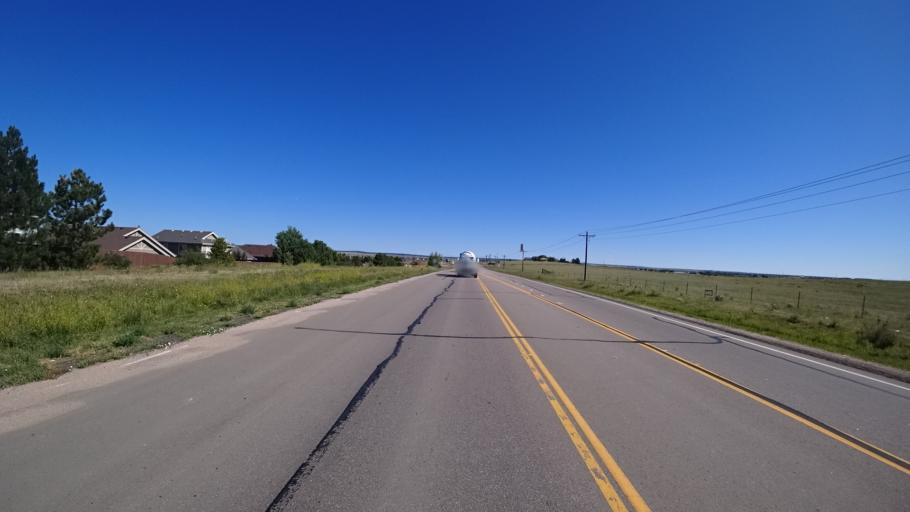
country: US
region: Colorado
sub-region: El Paso County
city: Cimarron Hills
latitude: 38.9089
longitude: -104.6830
